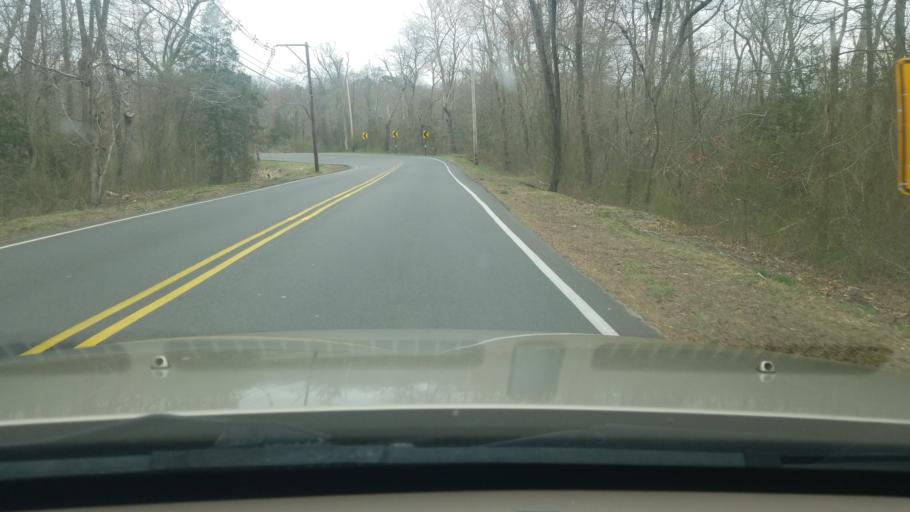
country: US
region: New Jersey
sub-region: Monmouth County
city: Ramtown
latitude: 40.1356
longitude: -74.1087
